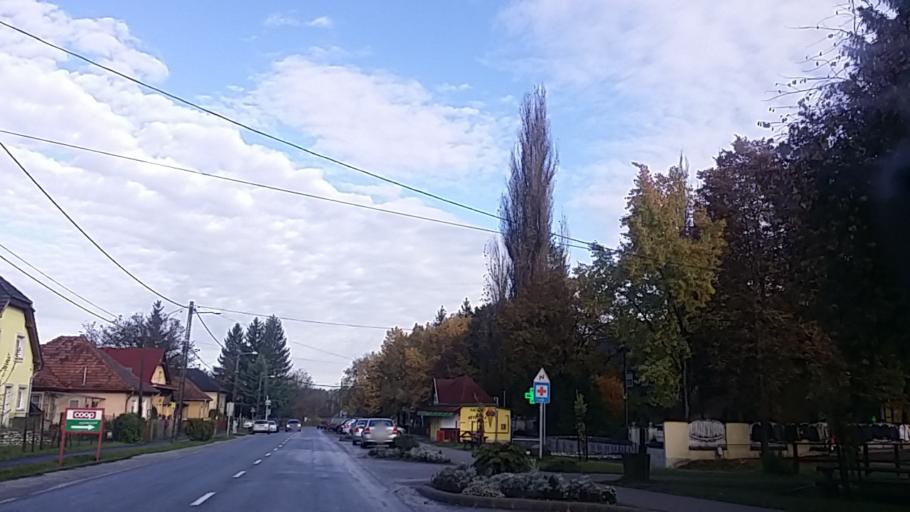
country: HU
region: Heves
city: Szilvasvarad
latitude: 48.1022
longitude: 20.3889
